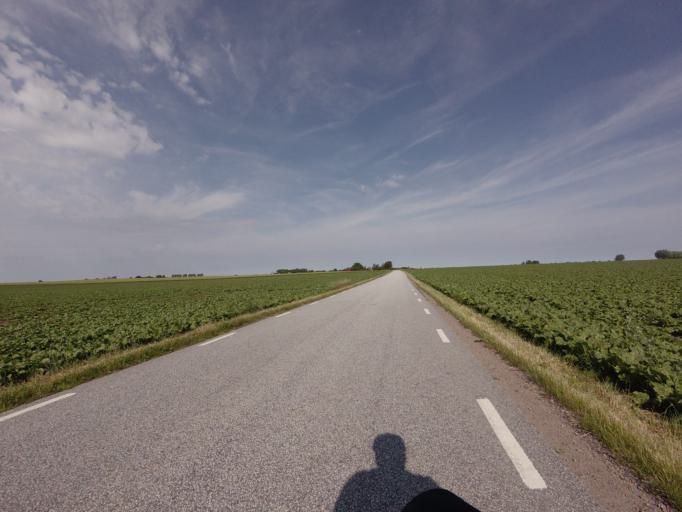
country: SE
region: Skane
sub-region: Vellinge Kommun
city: Vellinge
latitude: 55.4987
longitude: 13.0527
